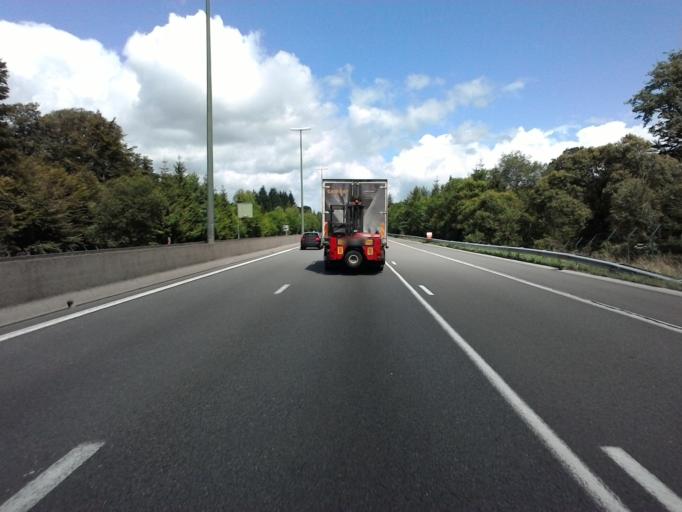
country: BE
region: Wallonia
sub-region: Province du Luxembourg
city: Leglise
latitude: 49.7517
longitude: 5.5672
